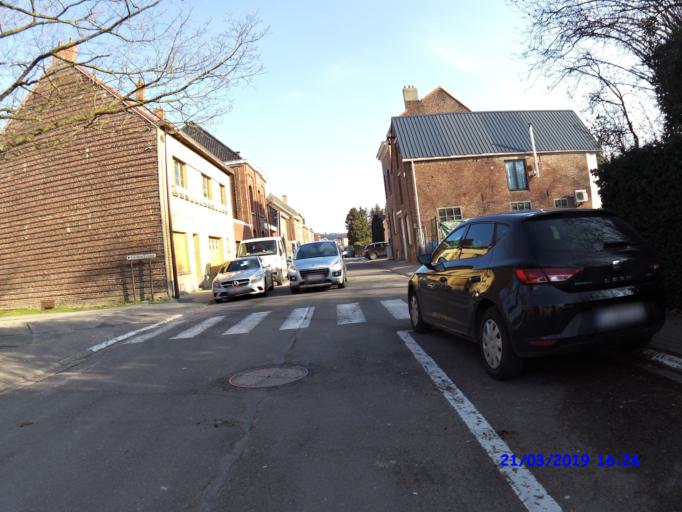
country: BE
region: Flanders
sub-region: Provincie Vlaams-Brabant
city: Beersel
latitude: 50.7509
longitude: 4.2687
